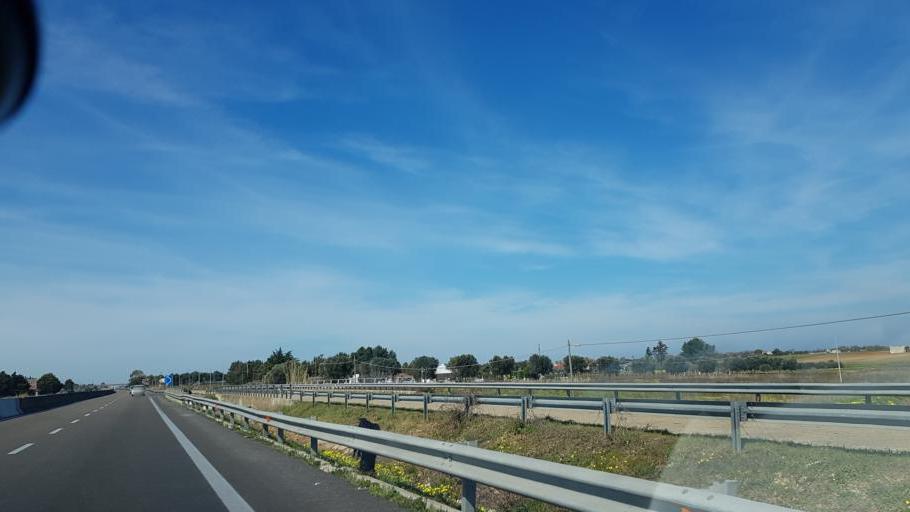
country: IT
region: Apulia
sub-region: Provincia di Brindisi
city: Brindisi
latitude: 40.6818
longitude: 17.8377
